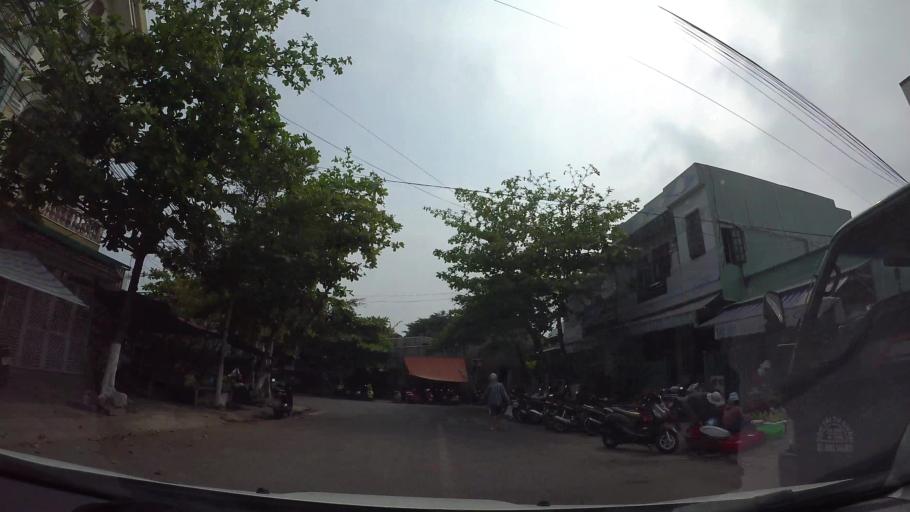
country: VN
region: Da Nang
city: Son Tra
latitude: 16.0919
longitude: 108.2456
